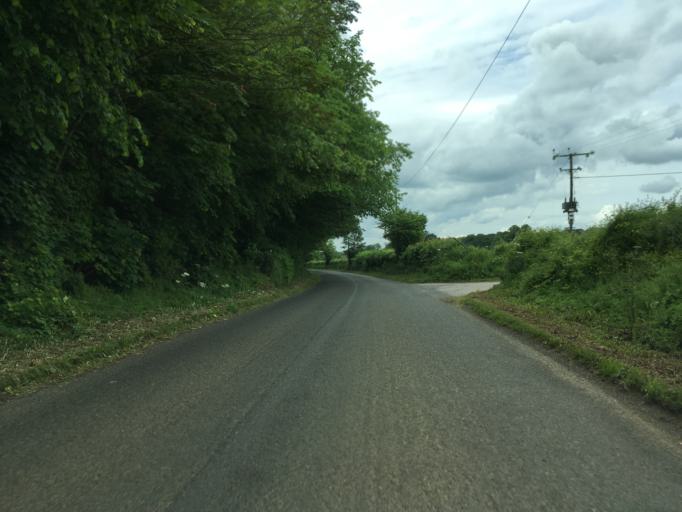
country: GB
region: England
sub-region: Wiltshire
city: Norton
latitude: 51.5226
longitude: -2.1914
